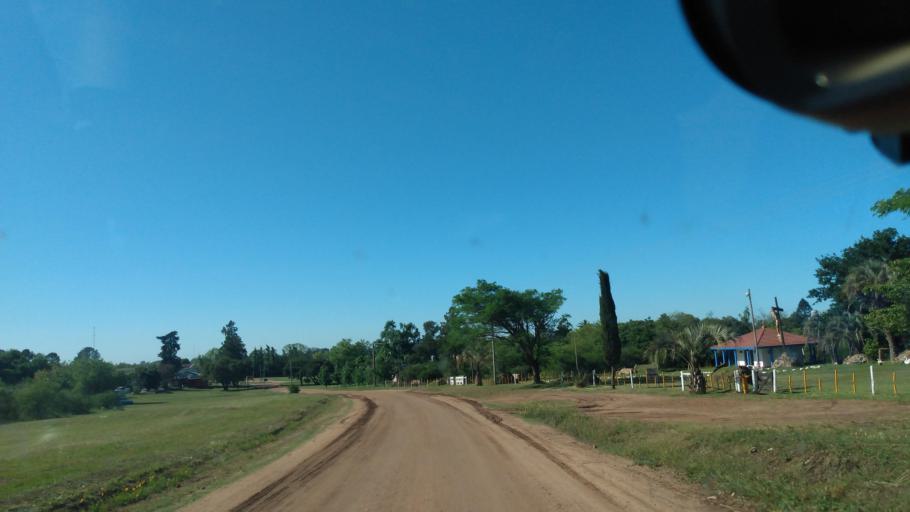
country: AR
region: Entre Rios
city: Colon
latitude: -32.1528
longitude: -58.1966
